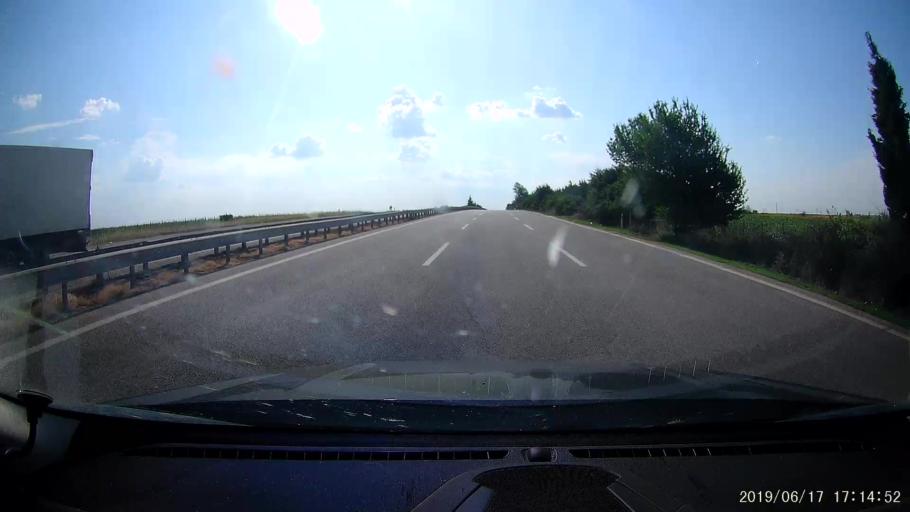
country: TR
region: Edirne
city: Edirne
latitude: 41.7003
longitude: 26.5081
